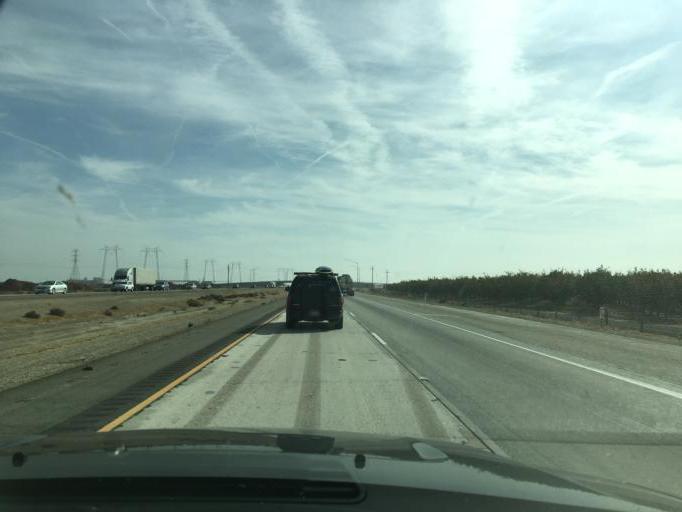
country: US
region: California
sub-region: Kern County
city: Buttonwillow
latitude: 35.5049
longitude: -119.5404
